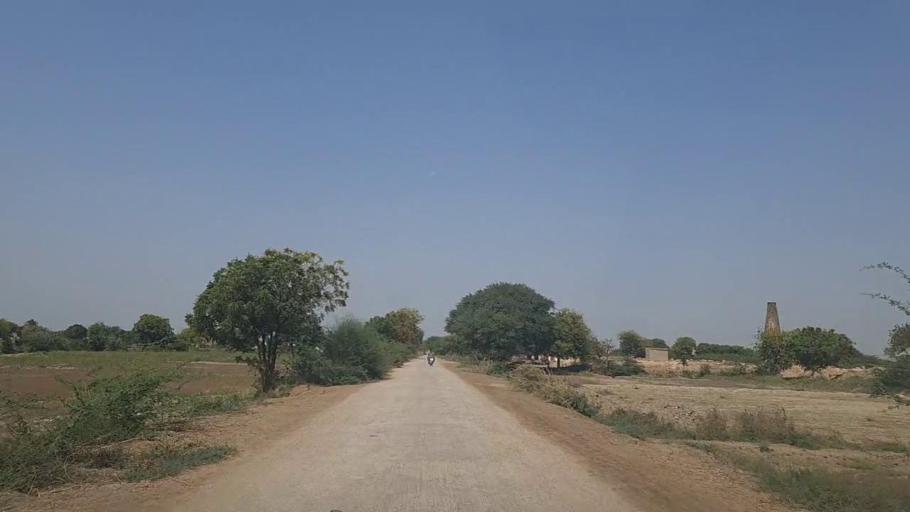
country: PK
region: Sindh
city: Naukot
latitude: 24.8446
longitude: 69.4395
